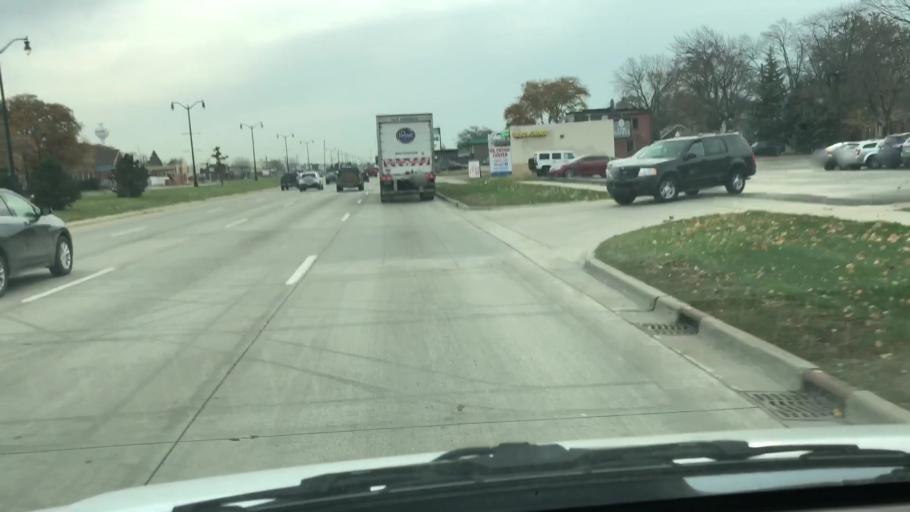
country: US
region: Michigan
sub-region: Wayne County
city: Allen Park
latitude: 42.2577
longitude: -83.2025
